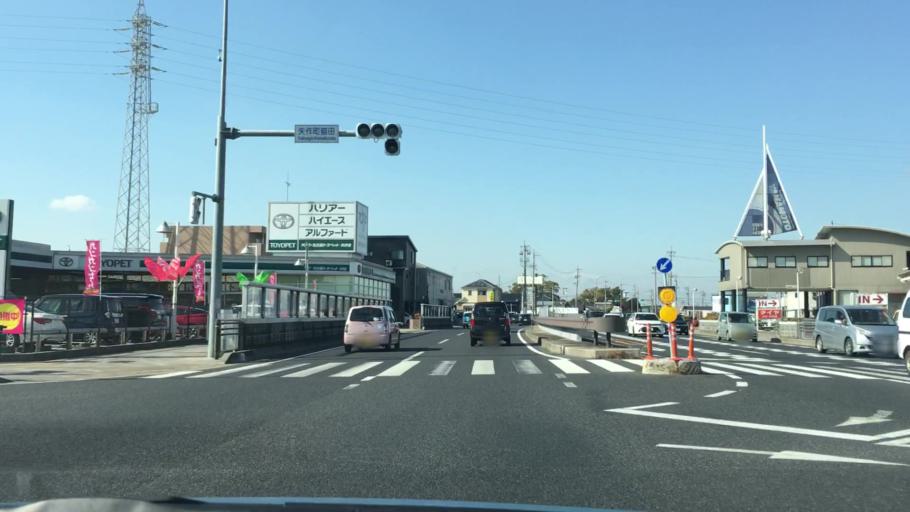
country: JP
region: Aichi
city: Okazaki
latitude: 34.9652
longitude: 137.1358
